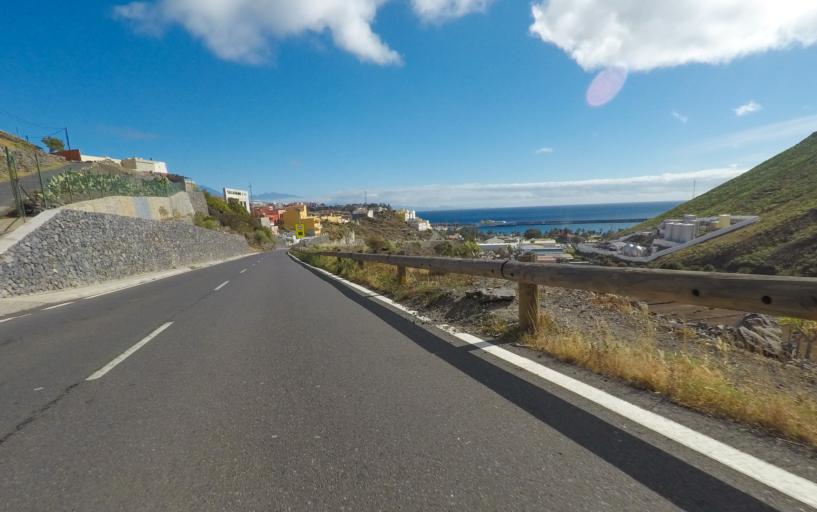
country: ES
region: Canary Islands
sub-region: Provincia de Santa Cruz de Tenerife
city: San Sebastian de la Gomera
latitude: 28.0899
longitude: -17.1213
